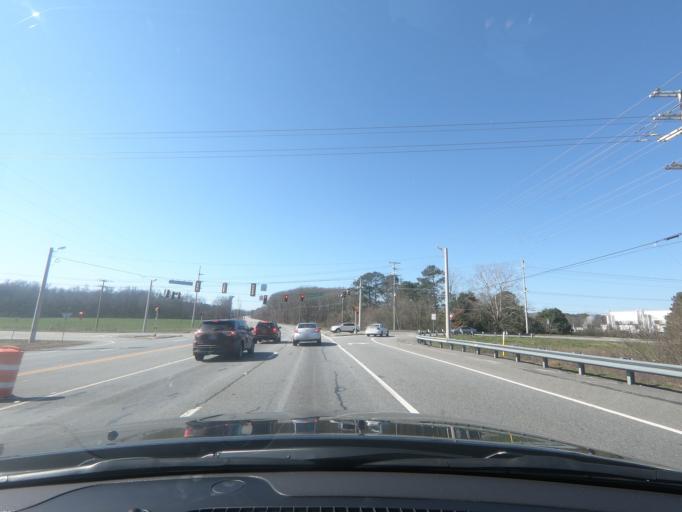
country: US
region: Georgia
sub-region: Gordon County
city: Calhoun
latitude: 34.4791
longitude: -84.9584
